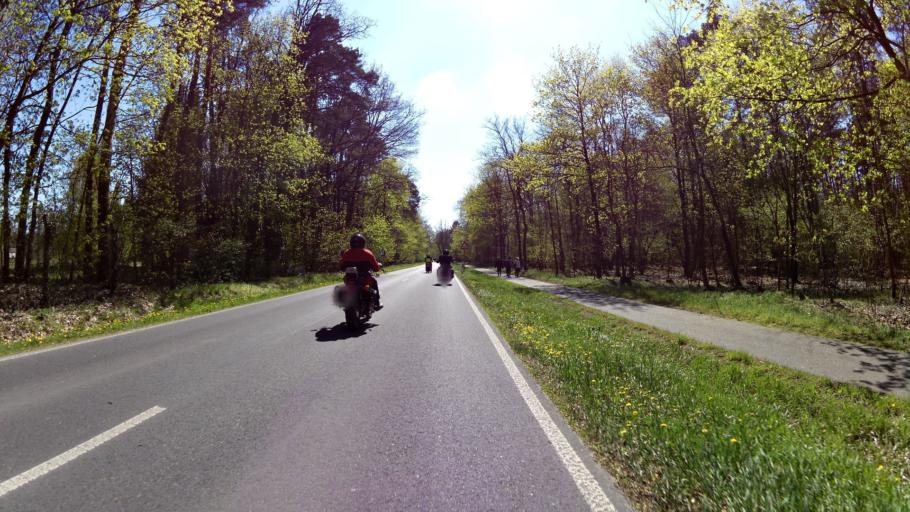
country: DE
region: Brandenburg
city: Waldsieversdorf
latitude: 52.5434
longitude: 14.0551
